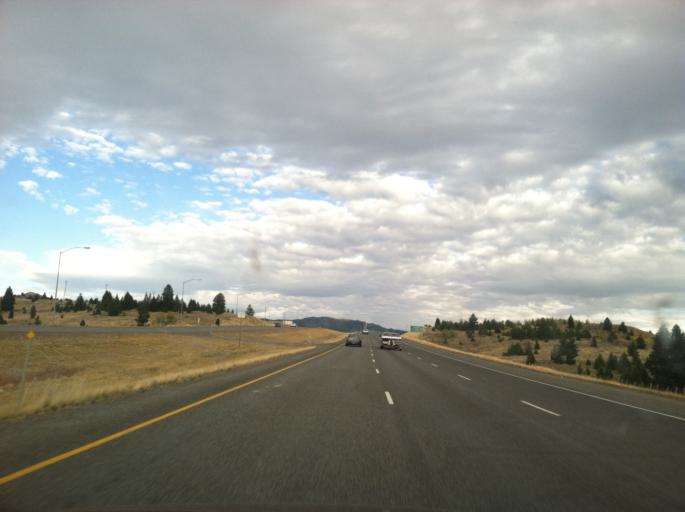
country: US
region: Montana
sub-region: Silver Bow County
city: Butte
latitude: 46.0061
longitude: -112.6011
